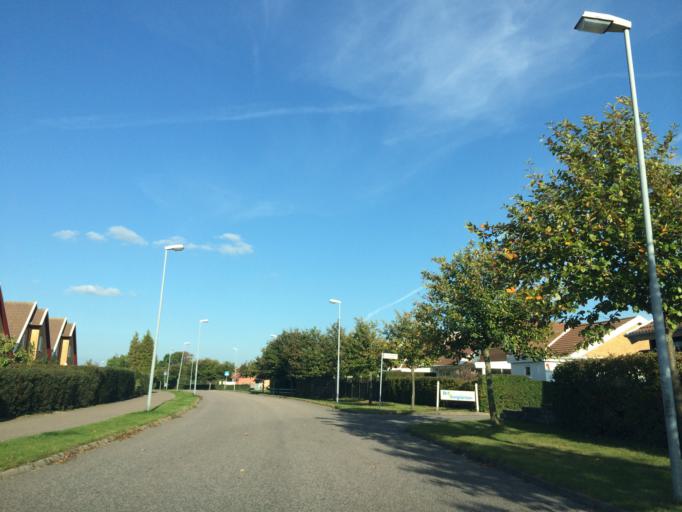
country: SE
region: Skane
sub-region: Kavlinge Kommun
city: Loddekopinge
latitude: 55.7620
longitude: 13.0254
